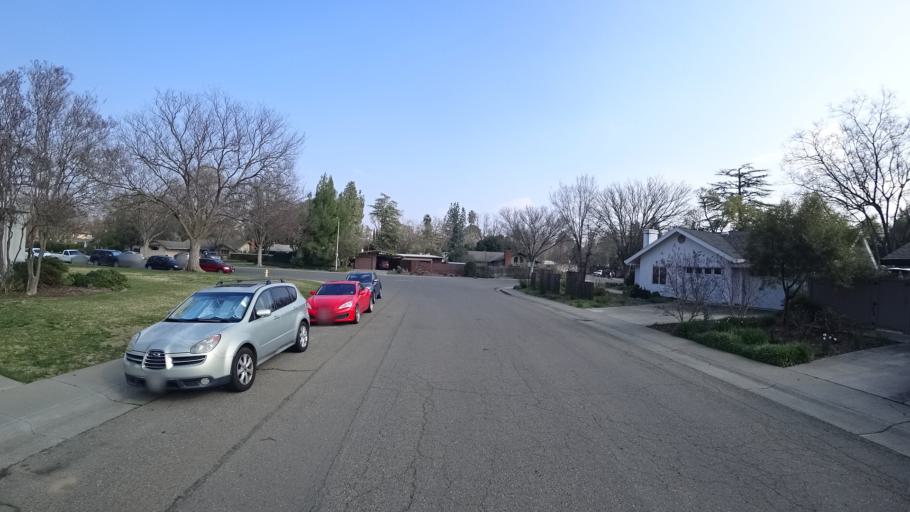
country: US
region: California
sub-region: Yolo County
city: Davis
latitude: 38.5498
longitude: -121.7551
